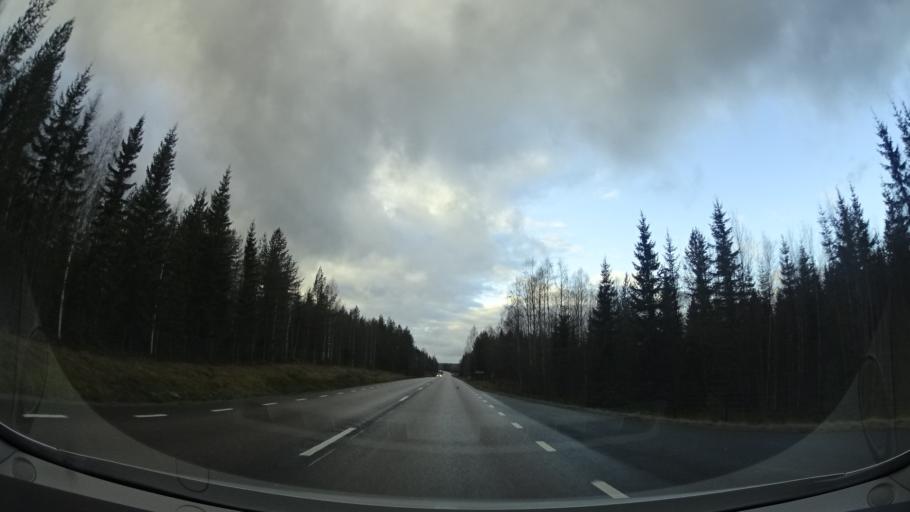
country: SE
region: Vaesterbotten
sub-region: Skelleftea Kommun
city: Forsbacka
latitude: 64.8071
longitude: 20.6937
